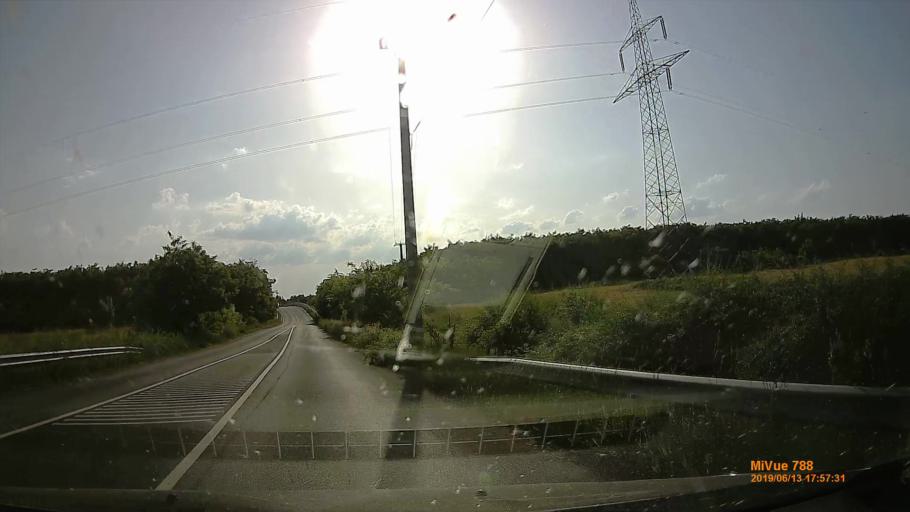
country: HU
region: Pest
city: Ecser
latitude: 47.4457
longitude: 19.3352
